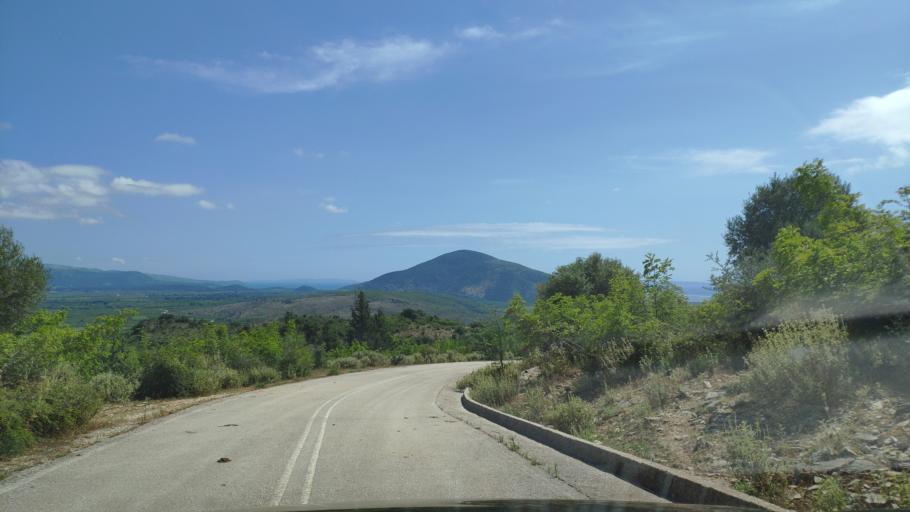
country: AL
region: Vlore
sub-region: Rrethi i Sarandes
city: Konispol
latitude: 39.6314
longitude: 20.2119
